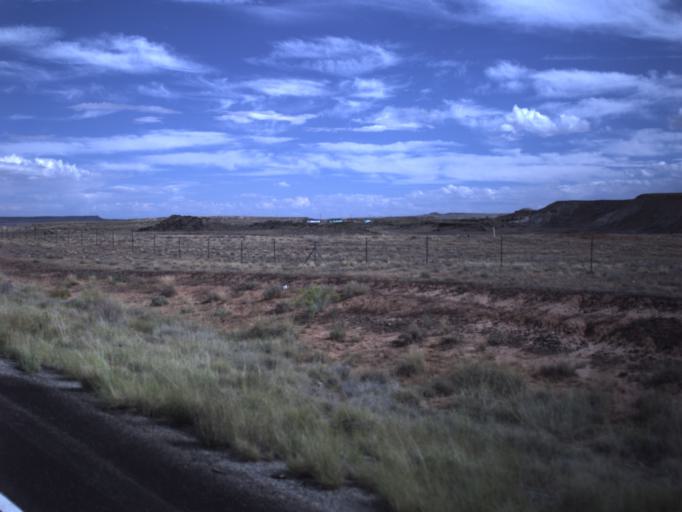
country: US
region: Colorado
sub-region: Montezuma County
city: Towaoc
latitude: 37.1718
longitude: -109.0924
